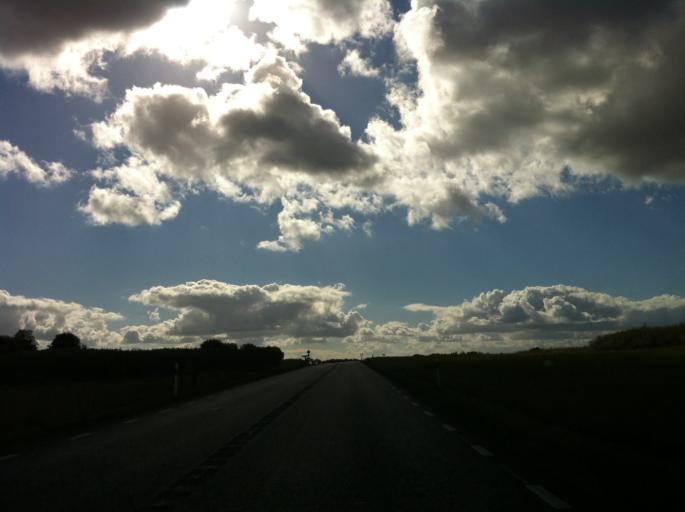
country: SE
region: Skane
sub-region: Tomelilla Kommun
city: Tomelilla
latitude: 55.6440
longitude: 14.0083
